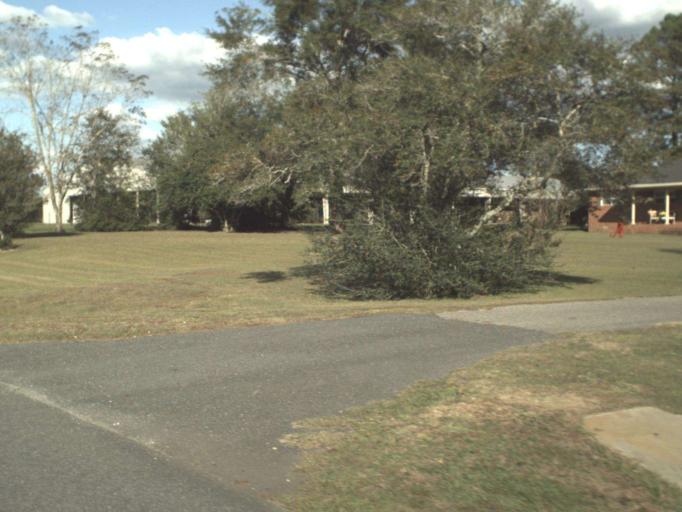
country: US
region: Florida
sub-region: Washington County
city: Chipley
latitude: 30.7306
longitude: -85.6108
